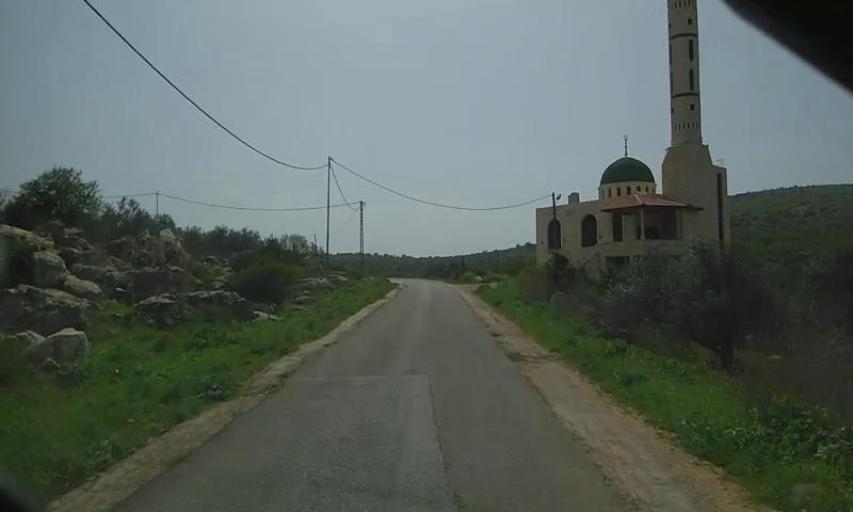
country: PS
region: West Bank
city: At Taybah
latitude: 32.5036
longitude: 35.1980
